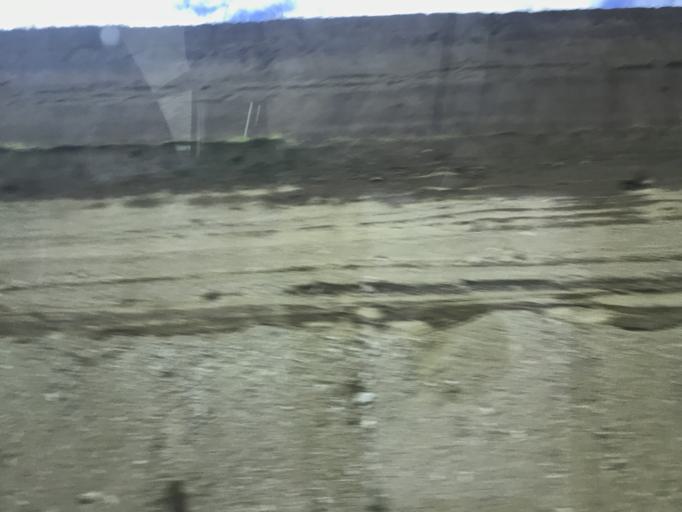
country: GT
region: Chimaltenango
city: El Tejar
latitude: 14.6354
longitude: -90.7931
